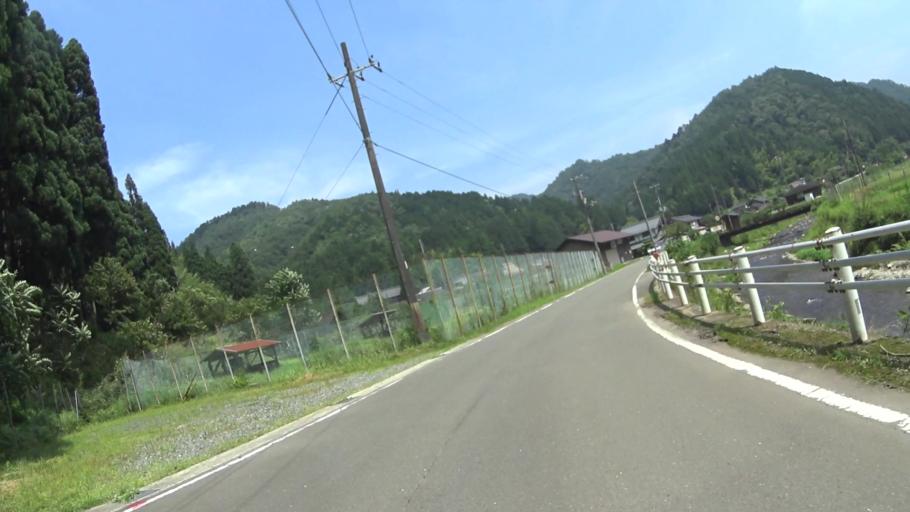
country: JP
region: Kyoto
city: Maizuru
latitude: 35.3139
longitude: 135.4376
